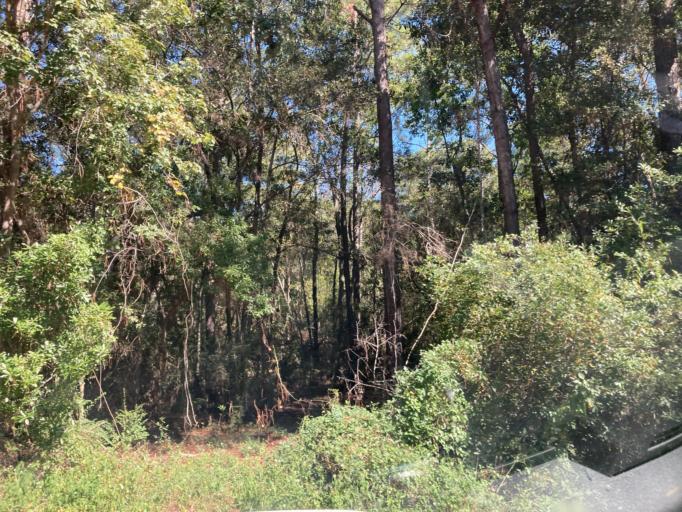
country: US
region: Mississippi
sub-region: Jackson County
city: Saint Martin
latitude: 30.4622
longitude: -88.8681
